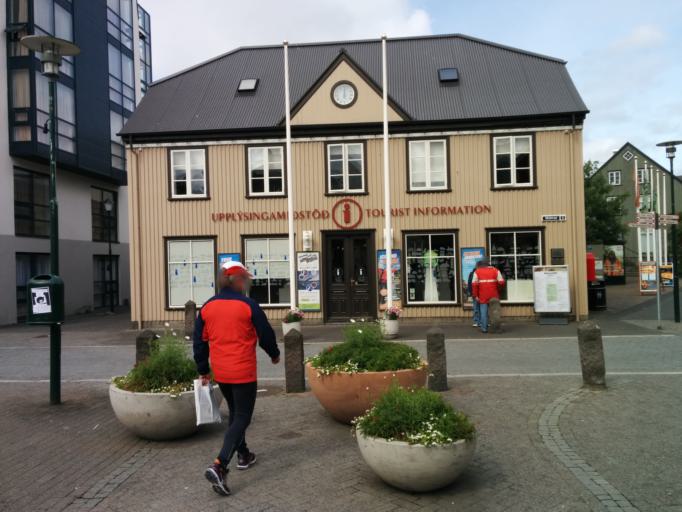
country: IS
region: Capital Region
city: Kopavogur
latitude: 64.1484
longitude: -21.9412
